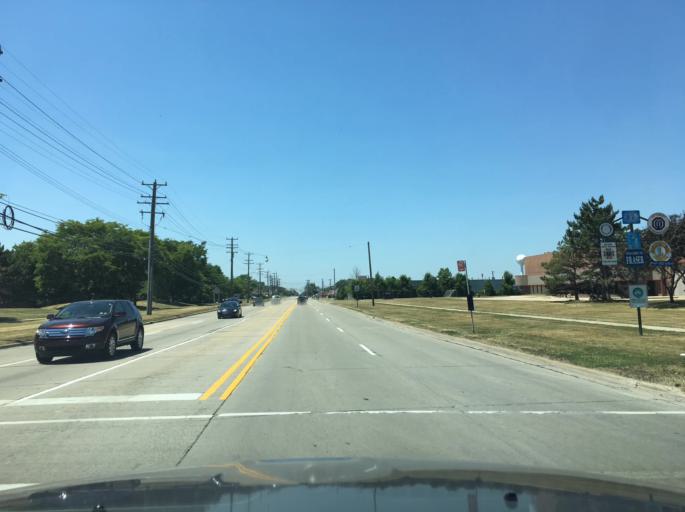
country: US
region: Michigan
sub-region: Macomb County
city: Fraser
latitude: 42.5394
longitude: -82.9297
